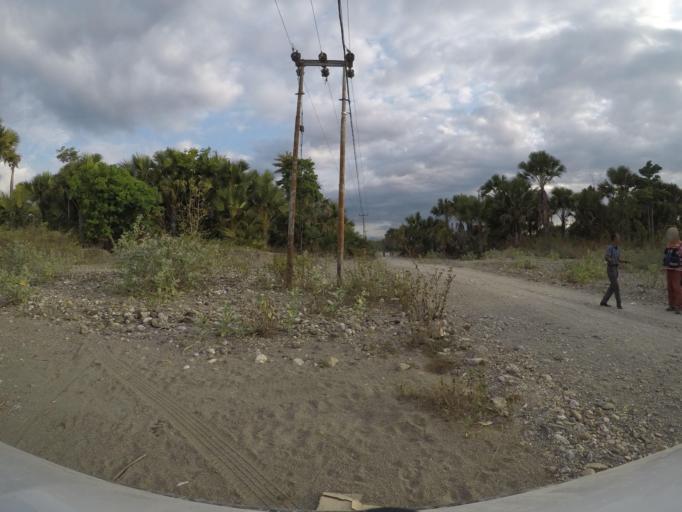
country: TL
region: Bobonaro
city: Maliana
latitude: -8.8598
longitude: 125.2173
